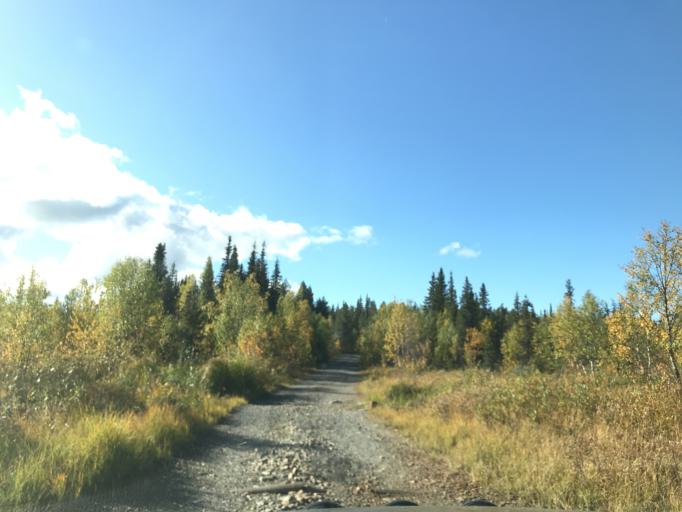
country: SE
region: Norrbotten
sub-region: Gallivare Kommun
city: Malmberget
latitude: 67.6465
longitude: 21.0828
